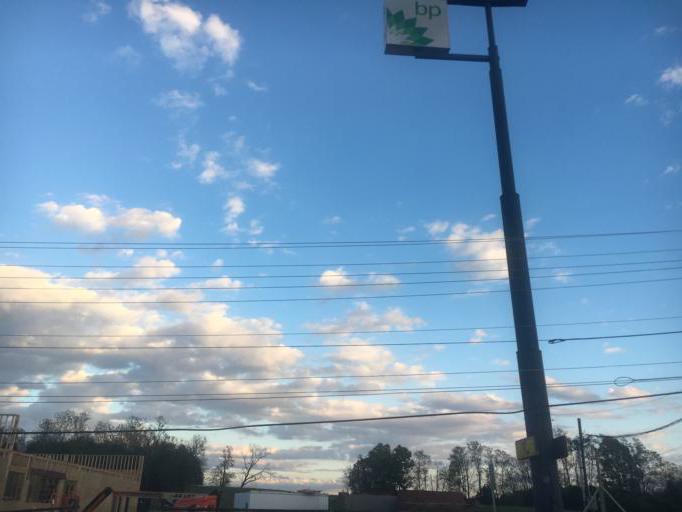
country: US
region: Tennessee
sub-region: Washington County
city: Gray
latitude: 36.4084
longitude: -82.4759
